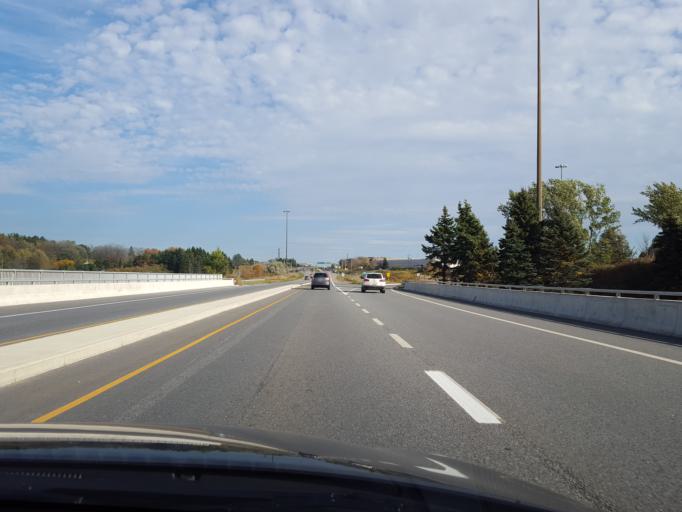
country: CA
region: Ontario
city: Ancaster
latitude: 43.2323
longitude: -79.9513
